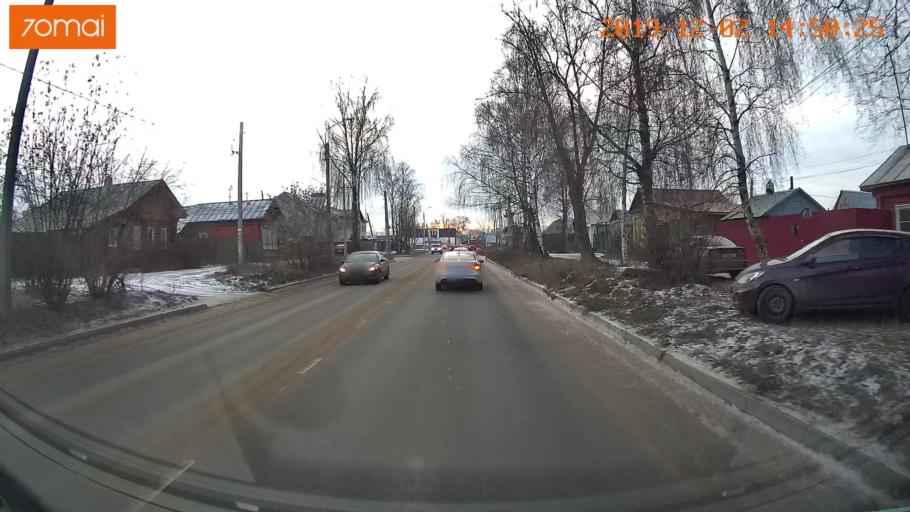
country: RU
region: Ivanovo
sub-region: Gorod Ivanovo
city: Ivanovo
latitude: 56.9800
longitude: 41.0052
